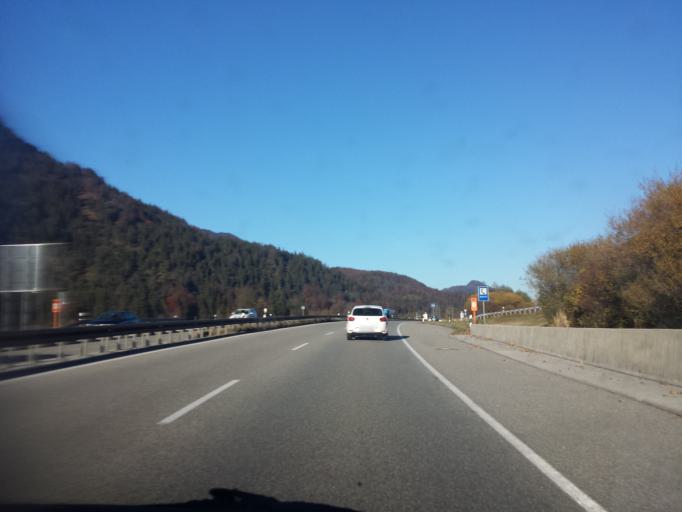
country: DE
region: Bavaria
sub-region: Upper Bavaria
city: Farchant
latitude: 47.5402
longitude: 11.1185
